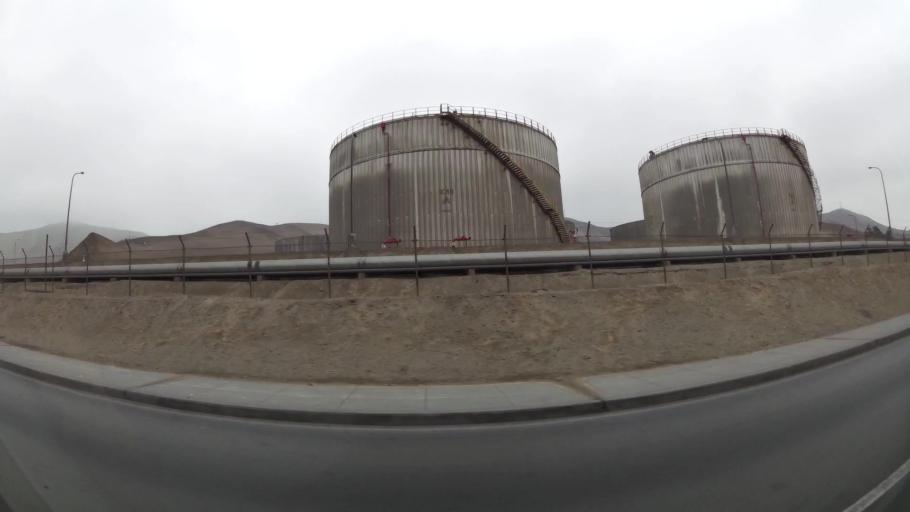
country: PE
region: Lima
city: Ventanilla
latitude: -11.9152
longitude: -77.1286
